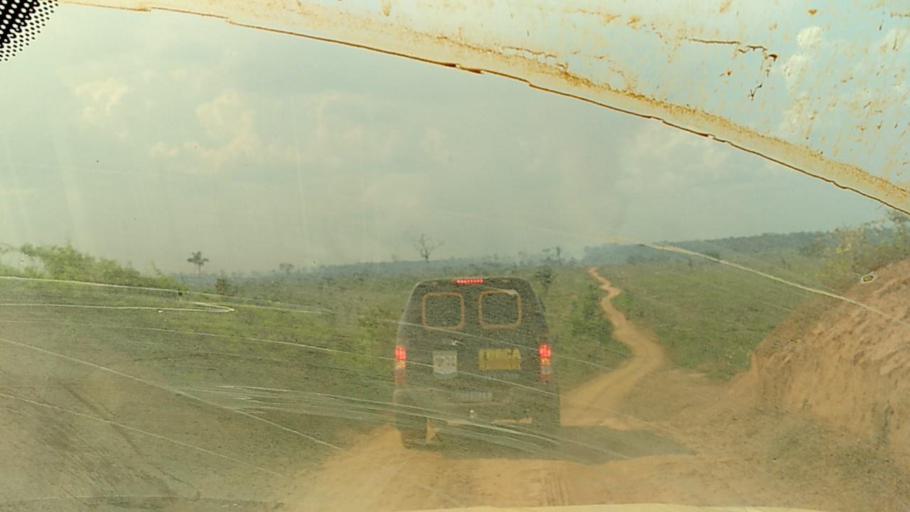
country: BR
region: Rondonia
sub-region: Porto Velho
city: Porto Velho
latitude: -8.6932
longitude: -63.2391
